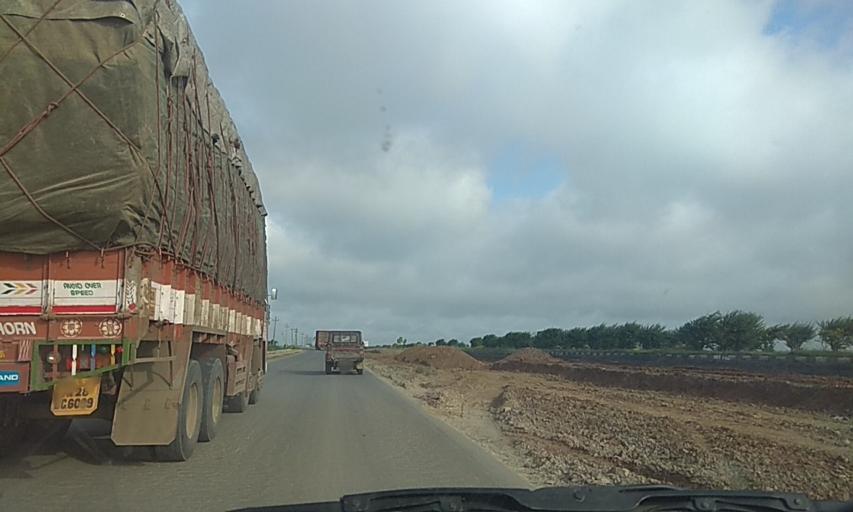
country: IN
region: Karnataka
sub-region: Haveri
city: Savanur
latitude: 14.8851
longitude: 75.3050
